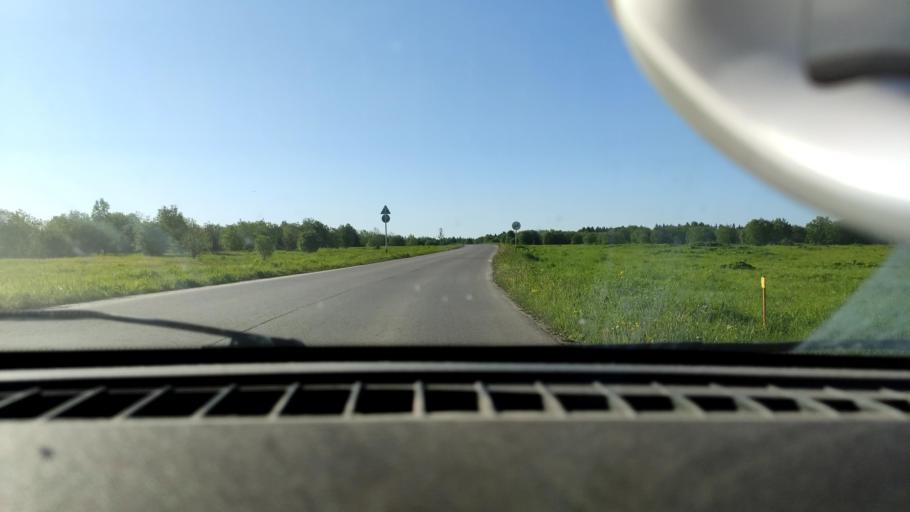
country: RU
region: Perm
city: Polazna
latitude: 58.2146
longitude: 56.4287
